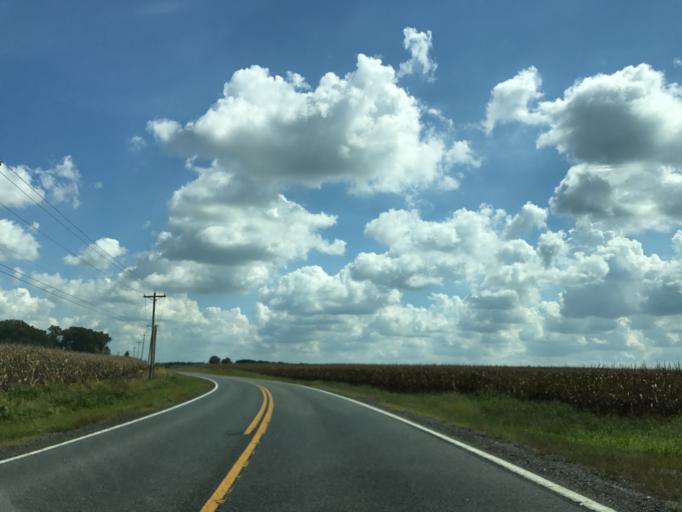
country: US
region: Maryland
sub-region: Queen Anne's County
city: Centreville
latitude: 39.0039
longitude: -75.9738
